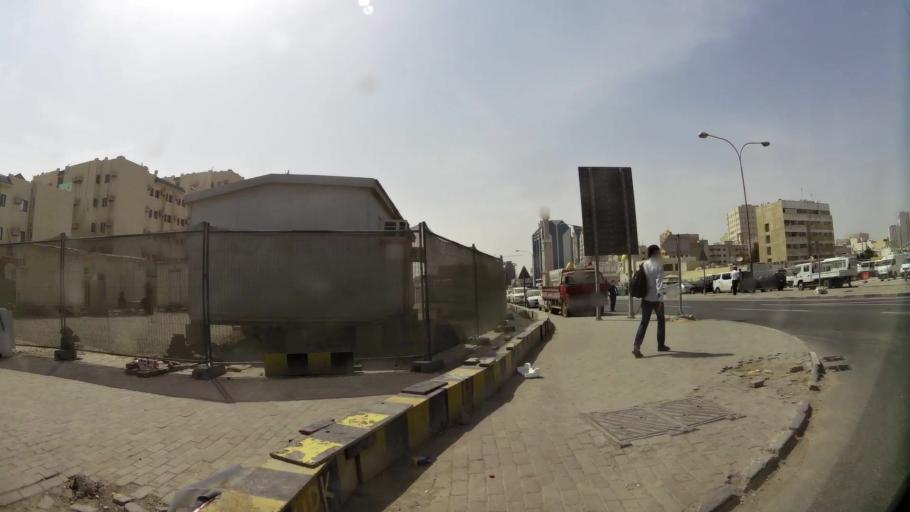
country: QA
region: Baladiyat ad Dawhah
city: Doha
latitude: 25.2795
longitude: 51.5341
